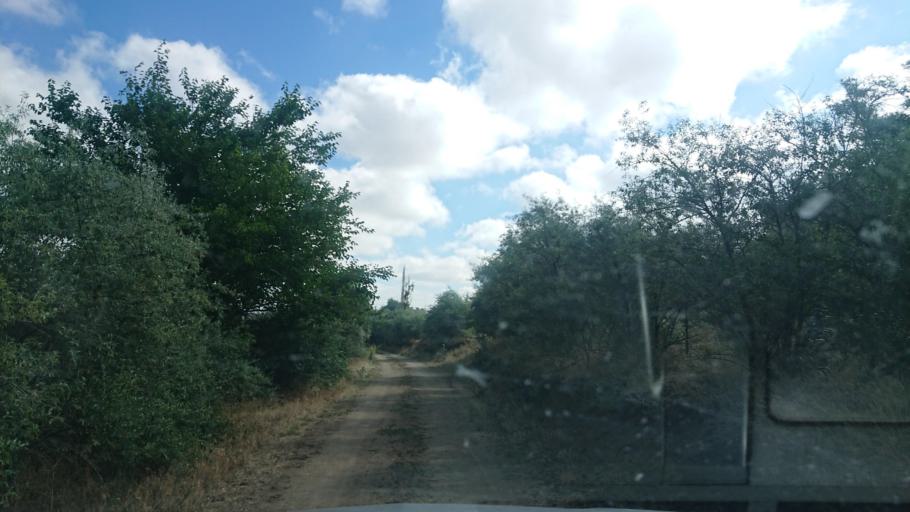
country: TR
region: Aksaray
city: Agacoren
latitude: 38.8498
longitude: 33.9323
